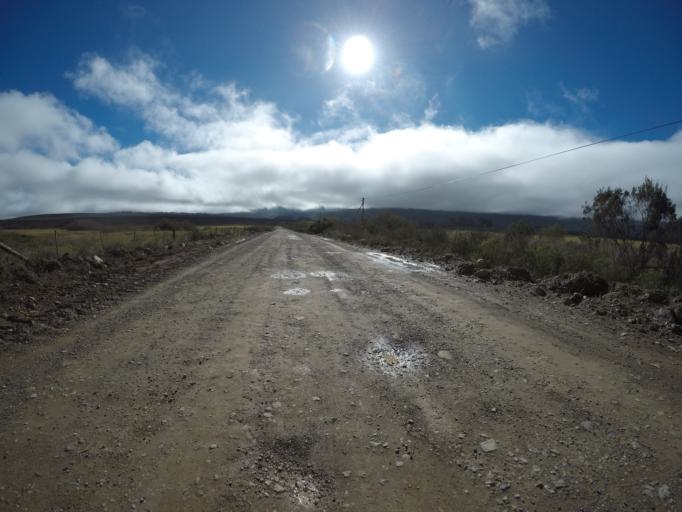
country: ZA
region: Western Cape
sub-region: Cape Winelands District Municipality
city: Ashton
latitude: -34.1263
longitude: 19.8398
